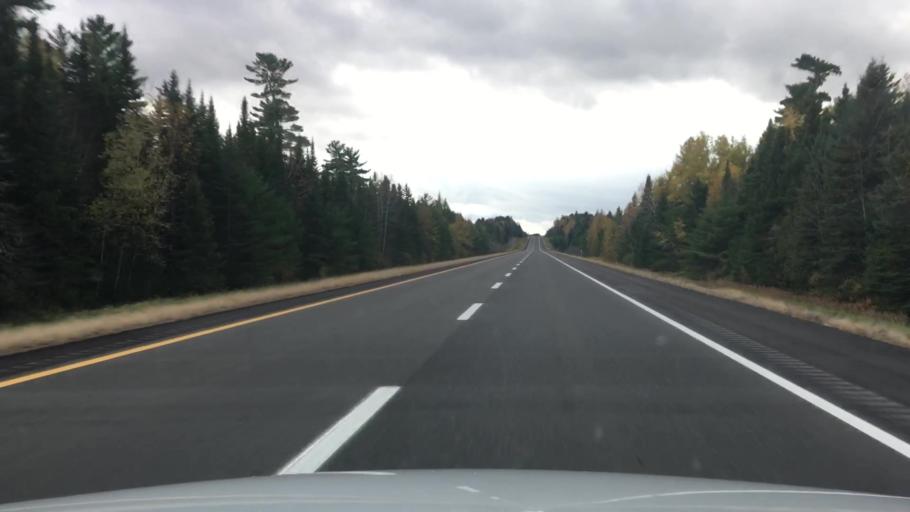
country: US
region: Maine
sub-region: Penobscot County
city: Patten
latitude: 46.0685
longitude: -68.2262
